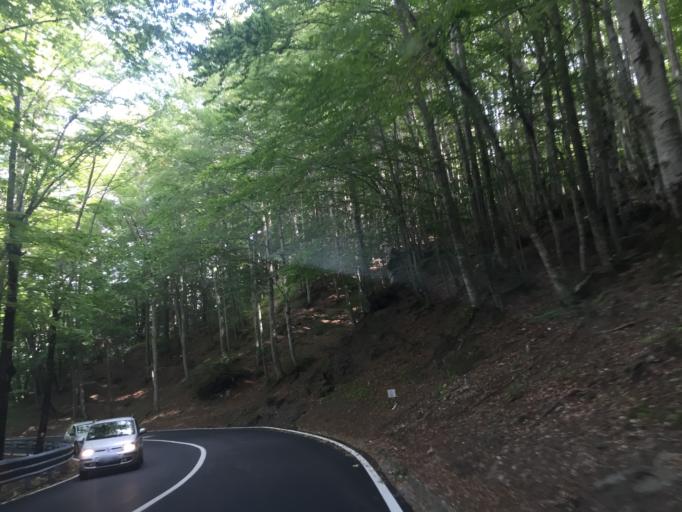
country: IT
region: Tuscany
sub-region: Provincia di Pistoia
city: Cutigliano
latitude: 44.1239
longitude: 10.7135
